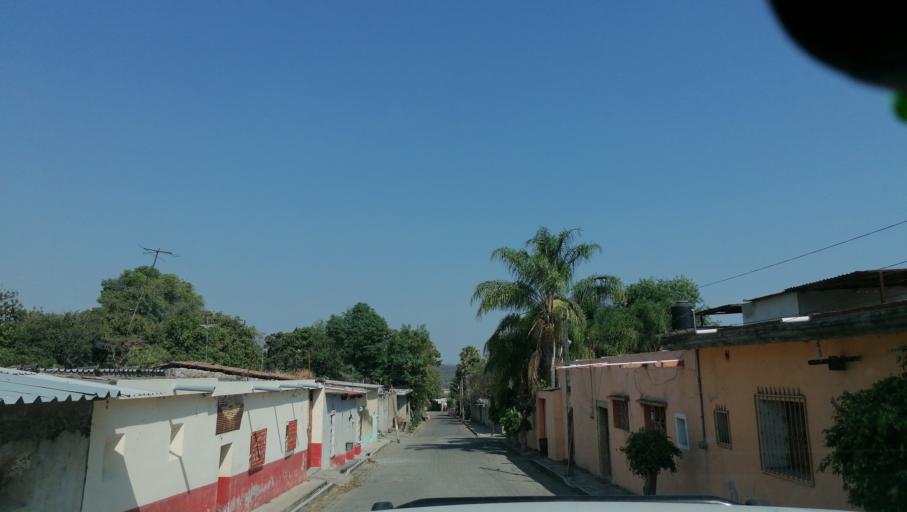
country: MX
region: Puebla
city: Huaquechula
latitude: 18.7721
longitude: -98.5399
